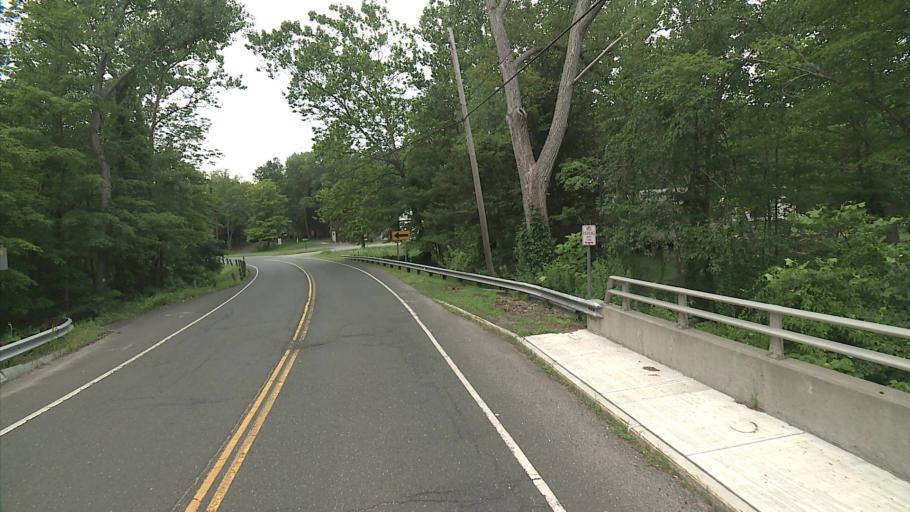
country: US
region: Connecticut
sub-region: Litchfield County
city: New Milford
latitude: 41.5583
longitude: -73.3313
